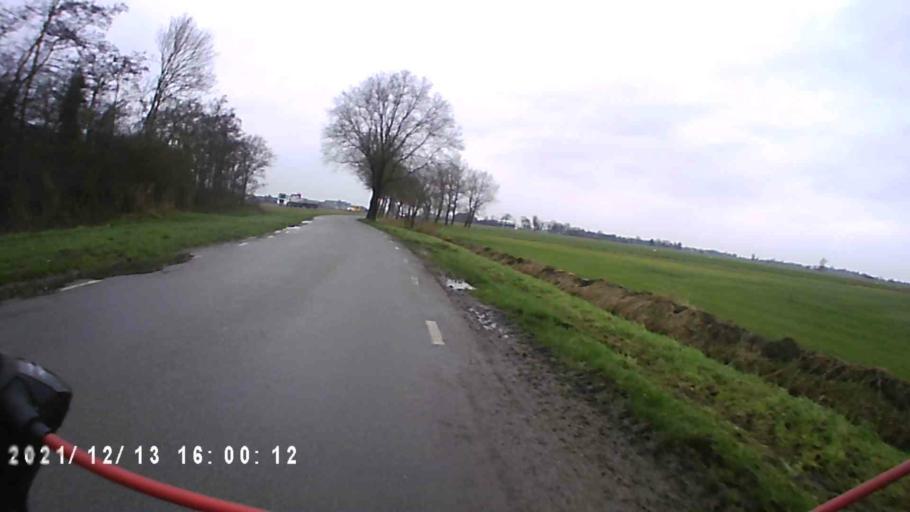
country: NL
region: Groningen
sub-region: Gemeente Appingedam
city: Appingedam
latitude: 53.3391
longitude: 6.8670
